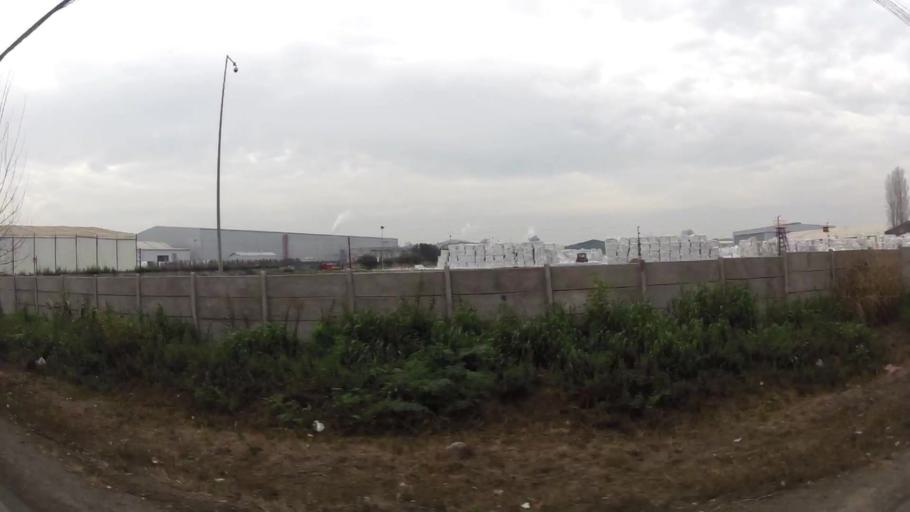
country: CL
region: Santiago Metropolitan
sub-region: Provincia de Chacabuco
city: Chicureo Abajo
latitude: -33.2664
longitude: -70.7524
